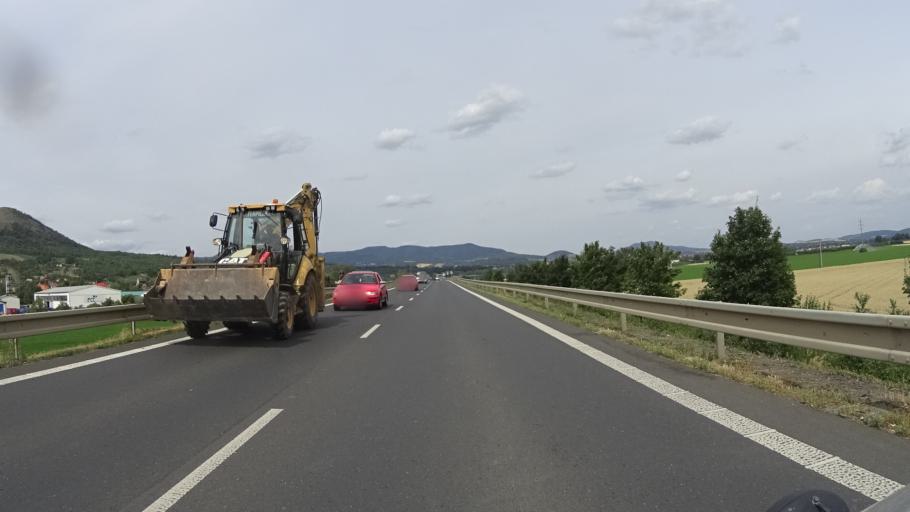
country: CZ
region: Ustecky
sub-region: Okres Litomerice
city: Litomerice
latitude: 50.5154
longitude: 14.0985
